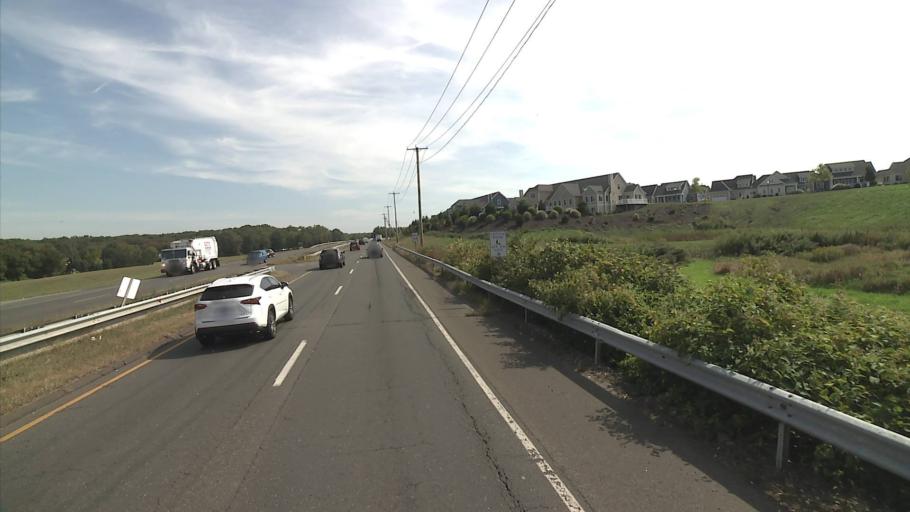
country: US
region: Connecticut
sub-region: New Haven County
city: Orange
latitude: 41.3109
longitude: -73.0453
